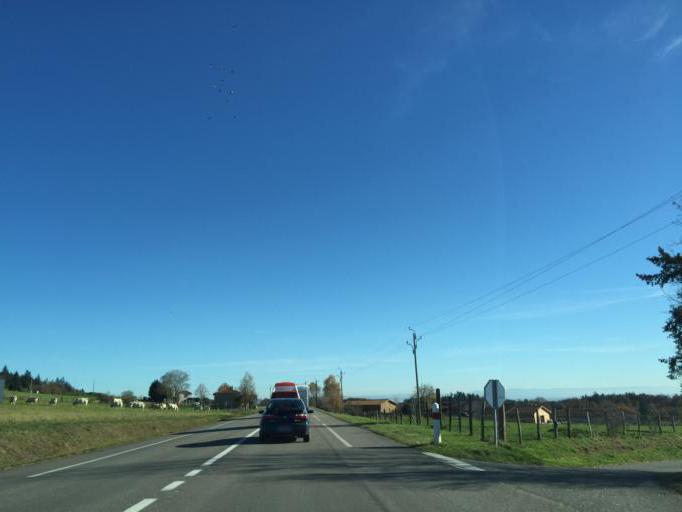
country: FR
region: Rhone-Alpes
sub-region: Departement de la Loire
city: Lentigny
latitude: 45.9125
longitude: 3.9854
